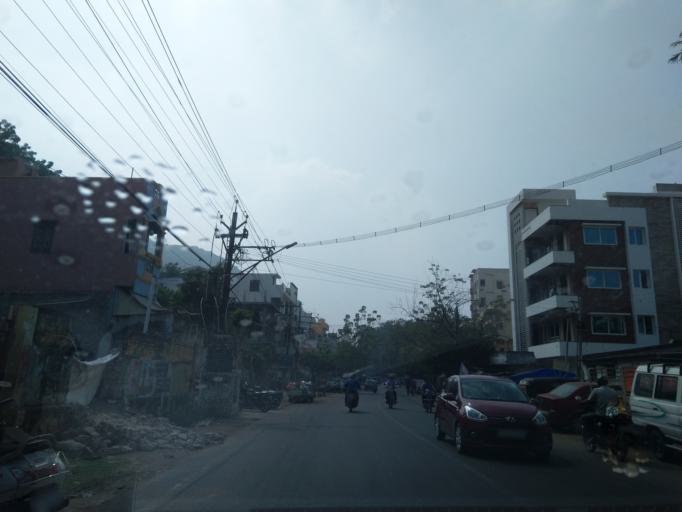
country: IN
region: Andhra Pradesh
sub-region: Krishna
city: Vijayawada
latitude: 16.5264
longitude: 80.6044
